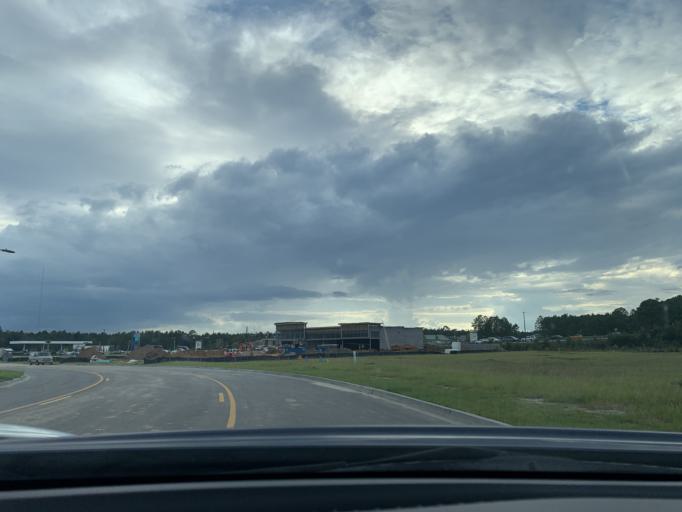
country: US
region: Georgia
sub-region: Chatham County
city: Pooler
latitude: 32.0812
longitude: -81.2796
